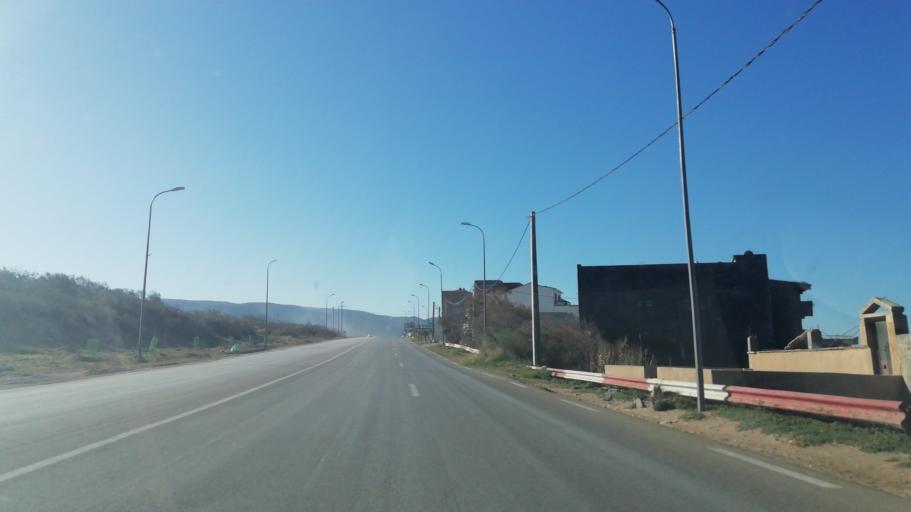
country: DZ
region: Oran
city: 'Ain el Turk
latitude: 35.7350
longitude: -0.8409
